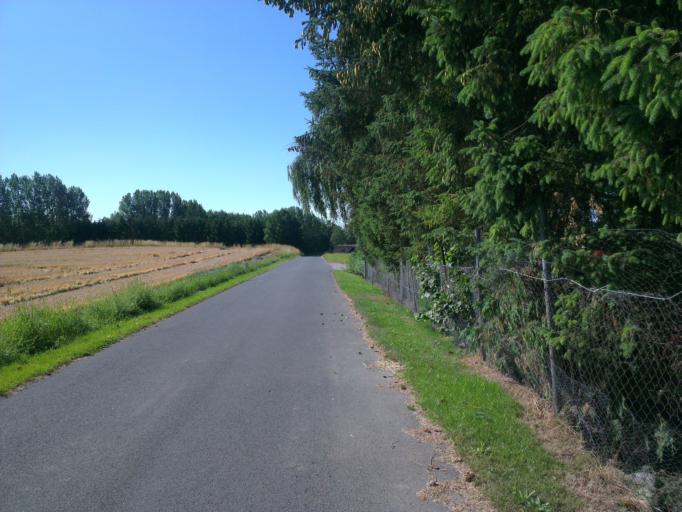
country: DK
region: Zealand
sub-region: Roskilde Kommune
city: Jyllinge
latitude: 55.7647
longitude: 12.0523
